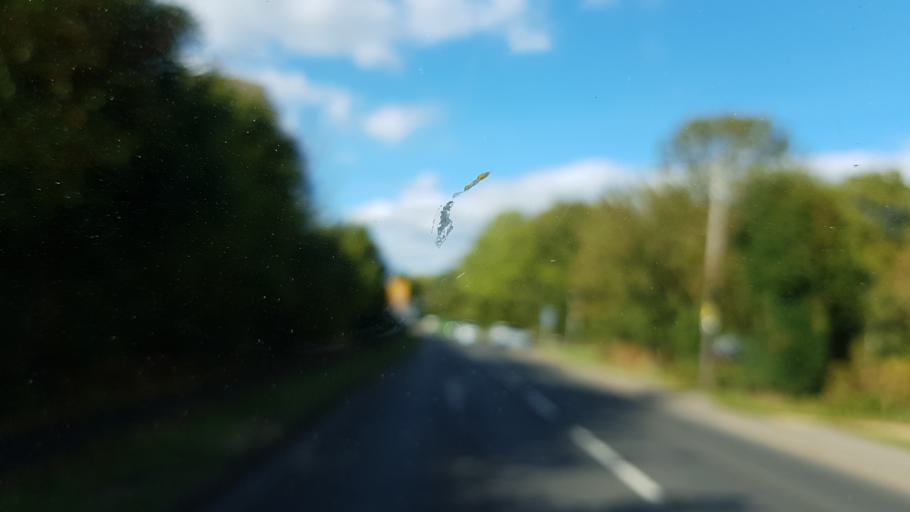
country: GB
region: England
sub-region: Surrey
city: Milford
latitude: 51.1606
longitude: -0.6491
